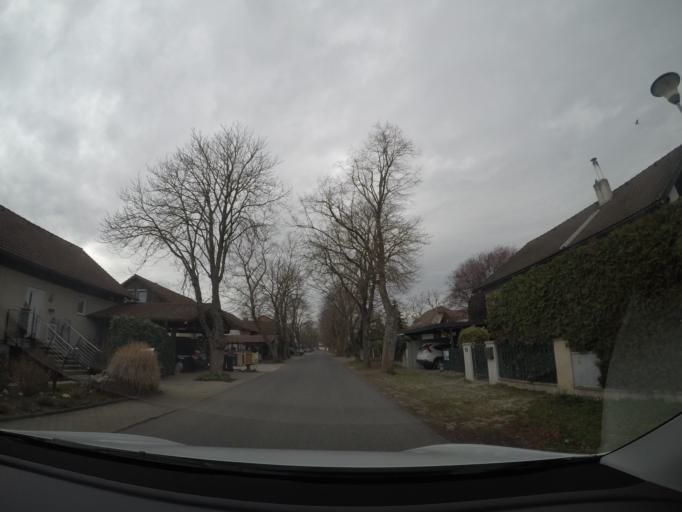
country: AT
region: Lower Austria
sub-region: Politischer Bezirk Baden
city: Ebreichsdorf
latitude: 47.9417
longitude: 16.3984
